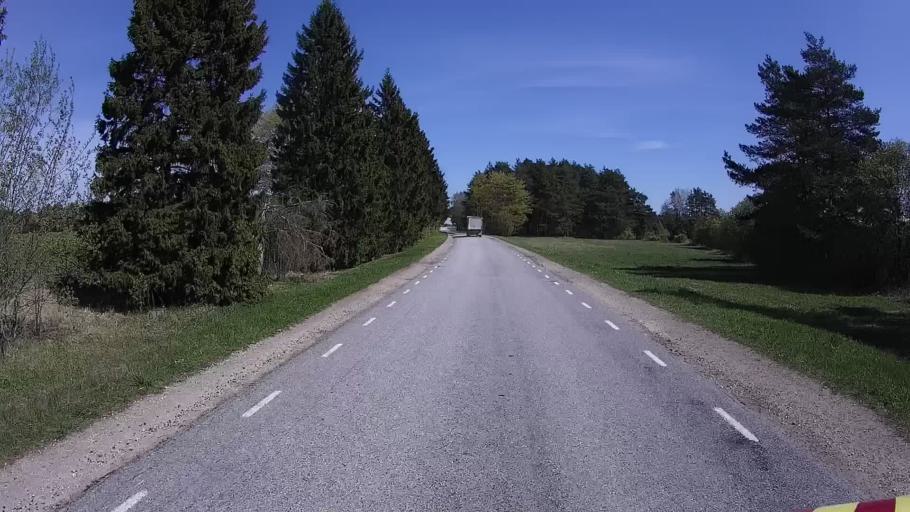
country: EE
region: Laeaene
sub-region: Ridala Parish
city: Uuemoisa
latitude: 58.9986
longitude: 23.7296
